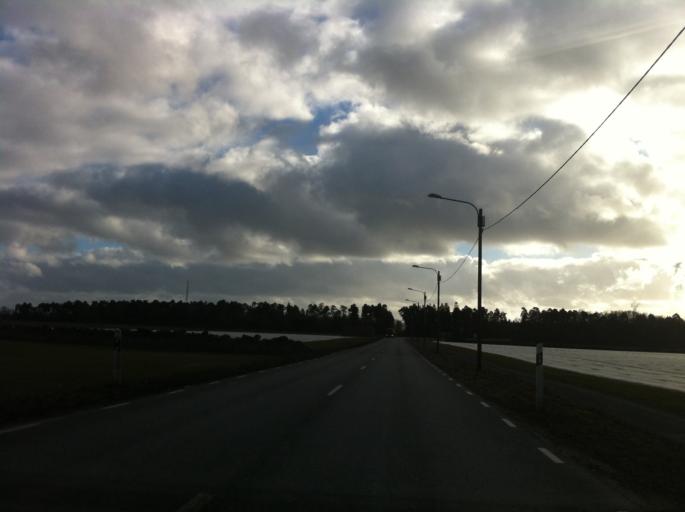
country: SE
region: Blekinge
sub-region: Solvesborgs Kommun
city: Soelvesborg
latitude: 56.0632
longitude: 14.5463
